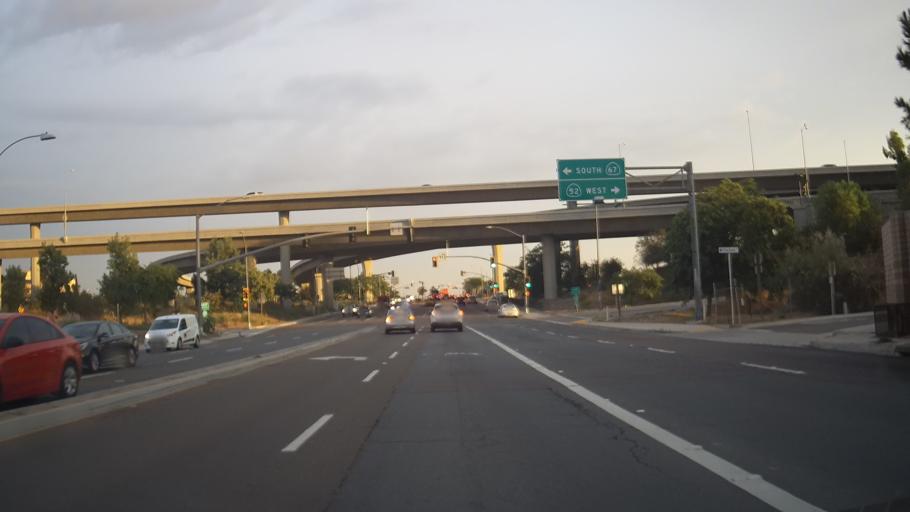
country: US
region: California
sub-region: San Diego County
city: Santee
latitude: 32.8337
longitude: -116.9647
